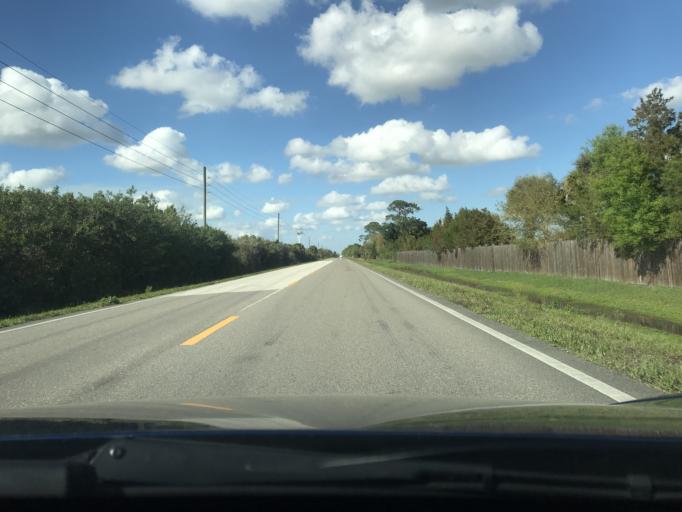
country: US
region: Florida
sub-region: Okeechobee County
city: Taylor Creek
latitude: 27.2166
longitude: -80.6942
